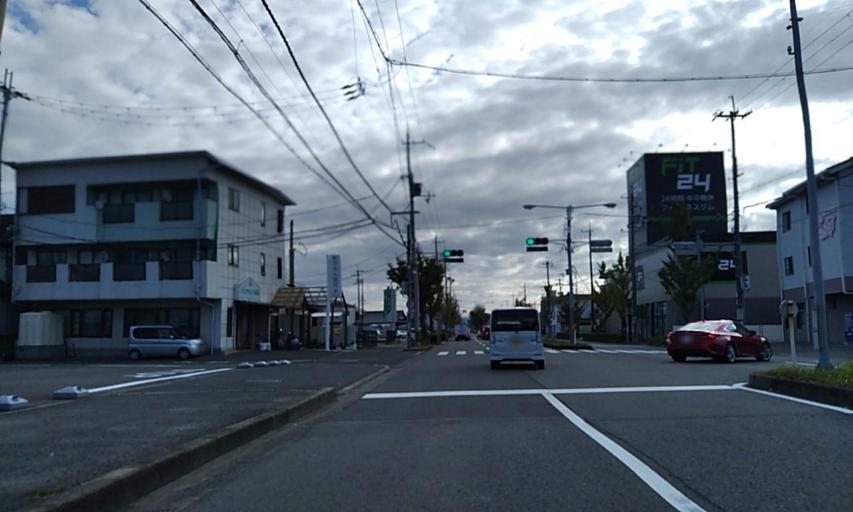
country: JP
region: Wakayama
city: Minato
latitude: 34.2548
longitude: 135.1349
